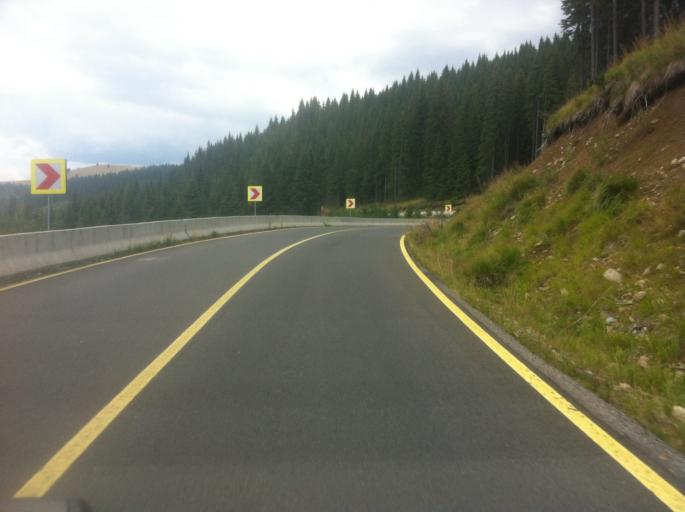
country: RO
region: Hunedoara
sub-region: Oras Petrila
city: Petrila
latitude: 45.4527
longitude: 23.6167
